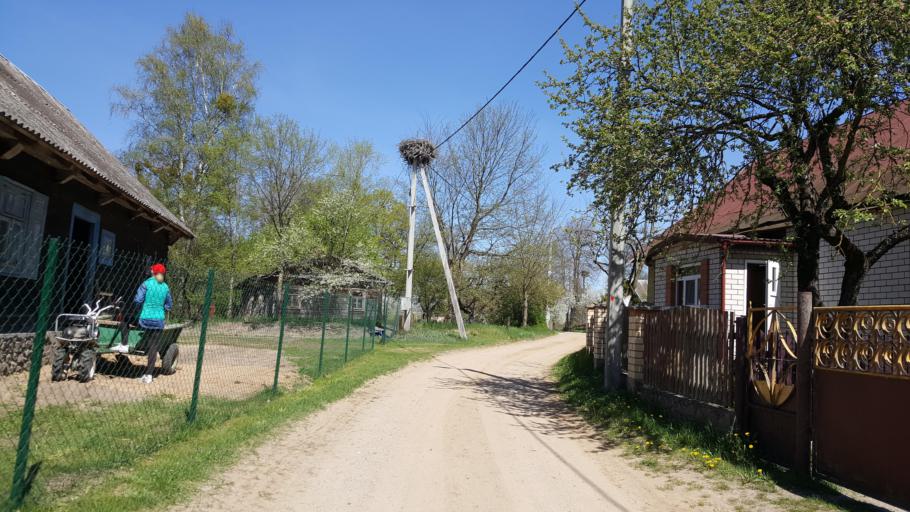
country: BY
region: Brest
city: Kamyanyets
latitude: 52.4256
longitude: 23.8450
